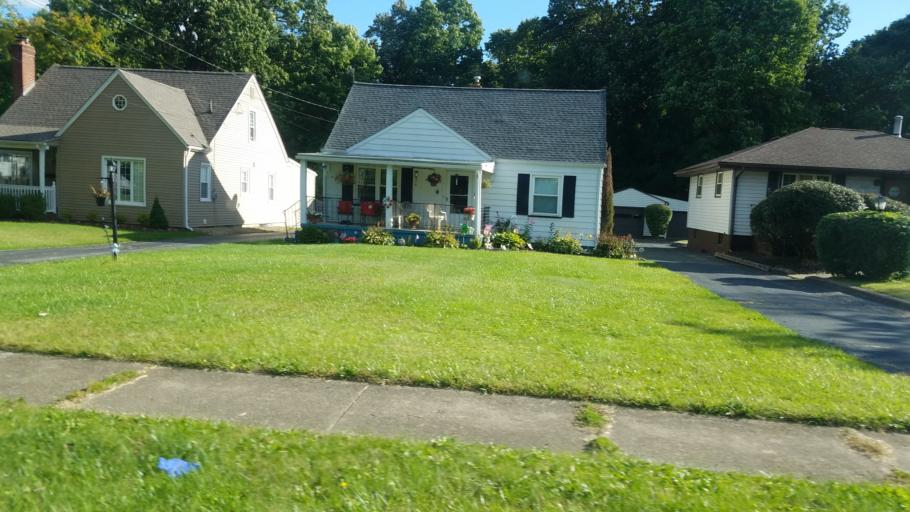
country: US
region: Ohio
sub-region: Mahoning County
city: Boardman
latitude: 41.0465
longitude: -80.6701
